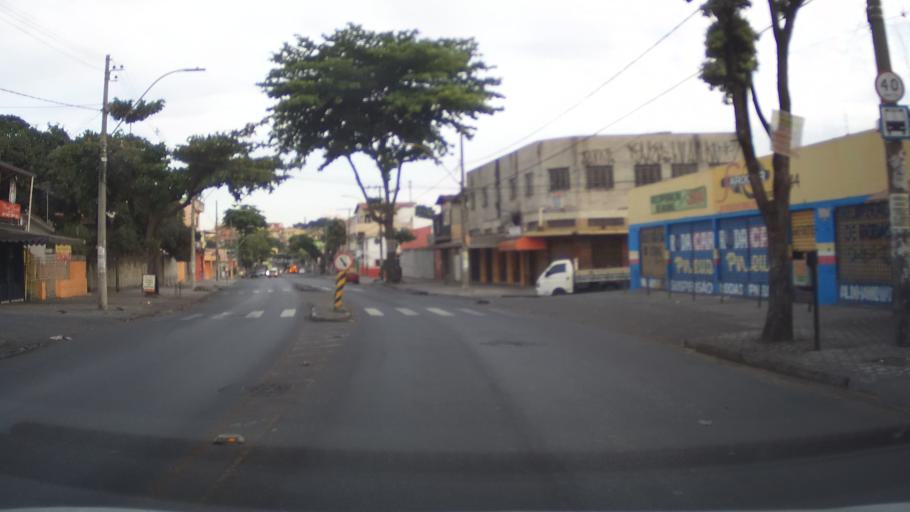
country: BR
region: Minas Gerais
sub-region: Contagem
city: Contagem
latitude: -19.9108
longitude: -44.0018
